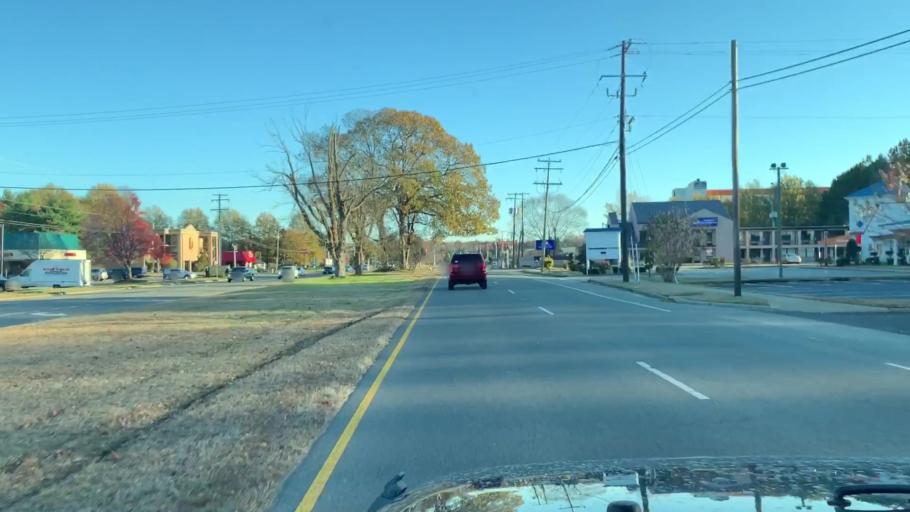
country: US
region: Virginia
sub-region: James City County
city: Williamsburg
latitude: 37.3428
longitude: -76.7564
